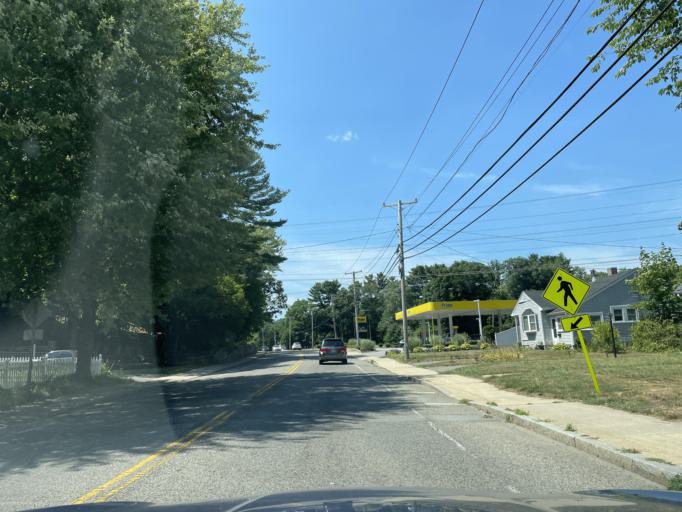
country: US
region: Massachusetts
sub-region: Norfolk County
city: Randolph
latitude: 42.1560
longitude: -71.0295
